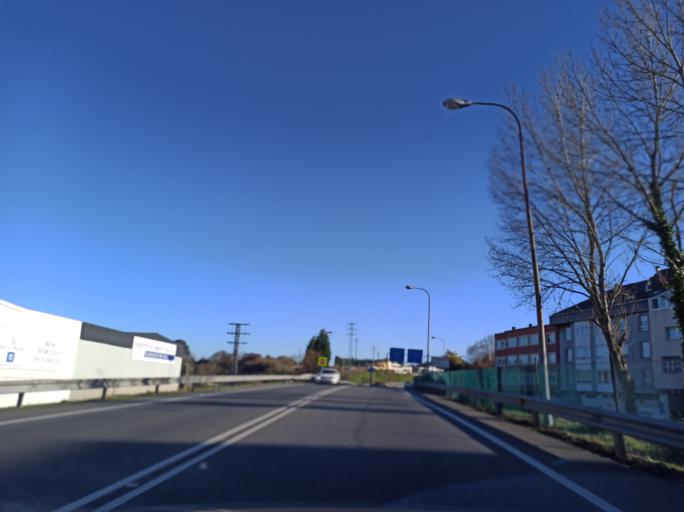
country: ES
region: Galicia
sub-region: Provincia da Coruna
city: Cambre
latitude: 43.3145
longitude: -8.3553
